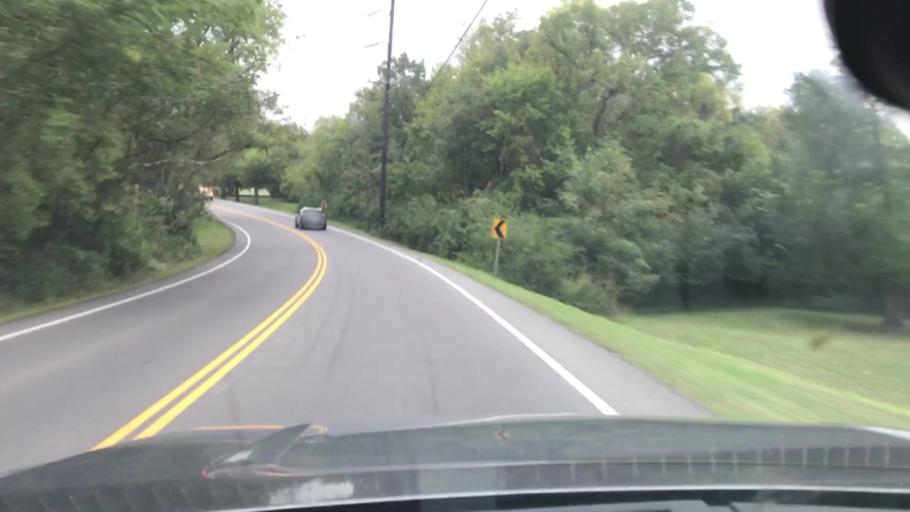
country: US
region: Tennessee
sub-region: Davidson County
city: Forest Hills
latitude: 36.0548
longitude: -86.9005
